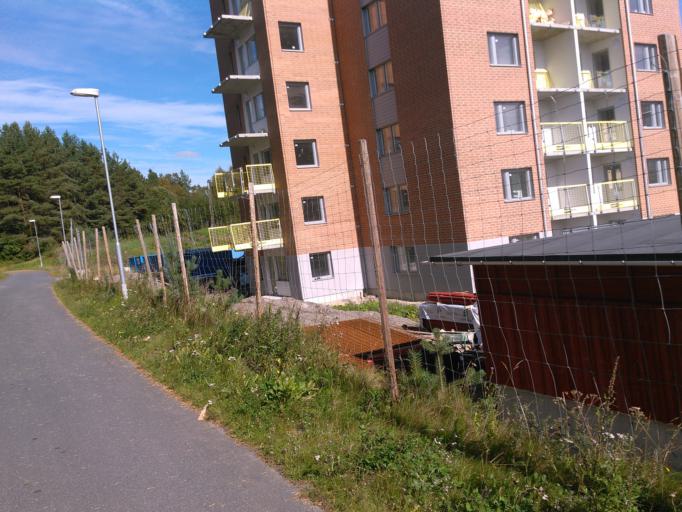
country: SE
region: Vaesterbotten
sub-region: Umea Kommun
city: Umea
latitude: 63.8001
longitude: 20.3108
